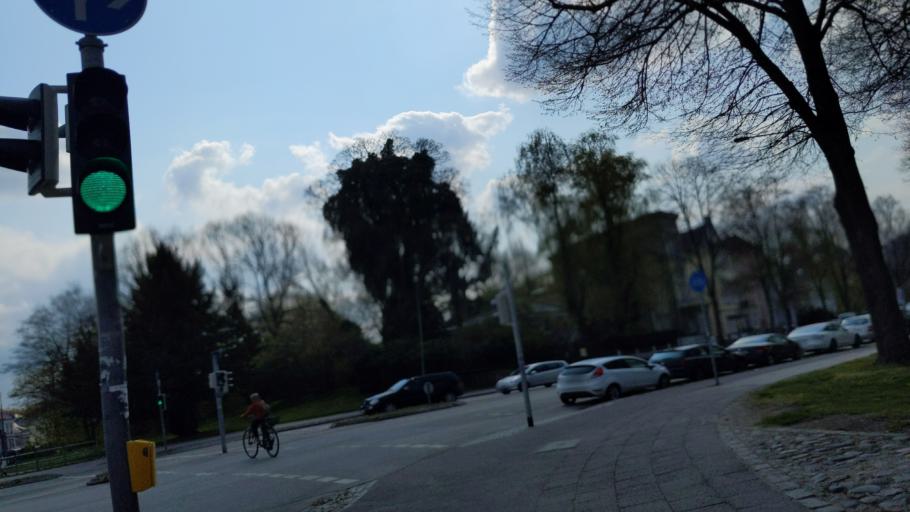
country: DE
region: Schleswig-Holstein
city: Luebeck
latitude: 53.8655
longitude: 10.6982
